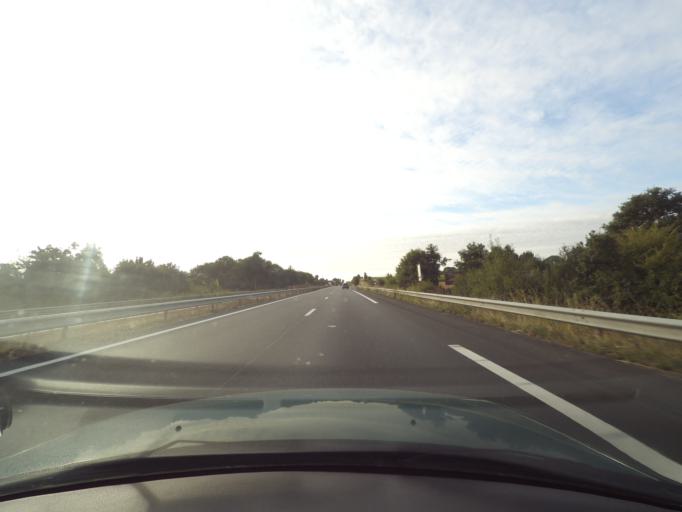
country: FR
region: Pays de la Loire
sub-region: Departement de Maine-et-Loire
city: Saint-Andre-de-la-Marche
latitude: 47.1003
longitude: -1.0212
